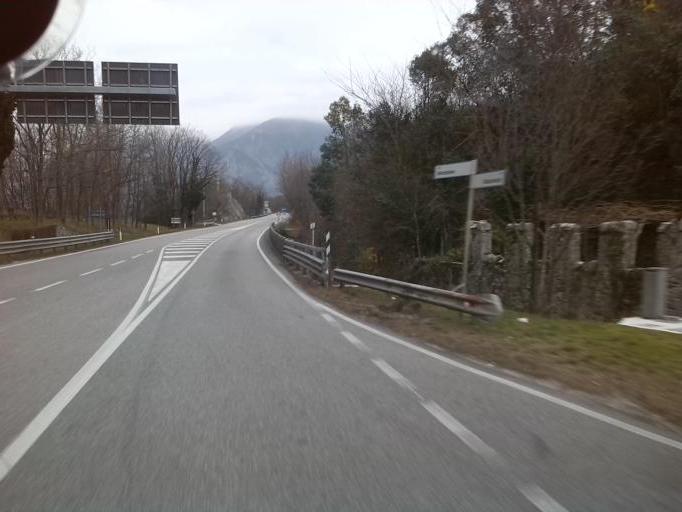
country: IT
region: Friuli Venezia Giulia
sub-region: Provincia di Udine
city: Bordano
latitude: 46.3024
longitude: 13.1200
